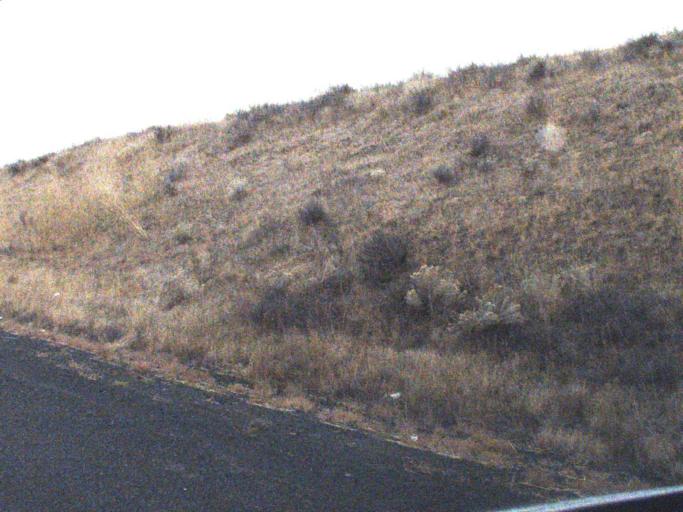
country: US
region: Washington
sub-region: Adams County
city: Ritzville
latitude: 46.7724
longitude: -118.3558
